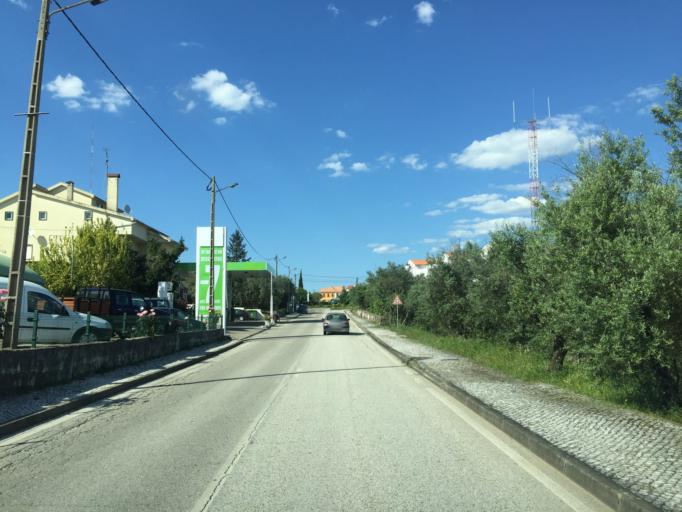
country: PT
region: Leiria
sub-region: Pedrogao Grande
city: Pedrogao Grande
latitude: 39.9123
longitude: -8.1496
